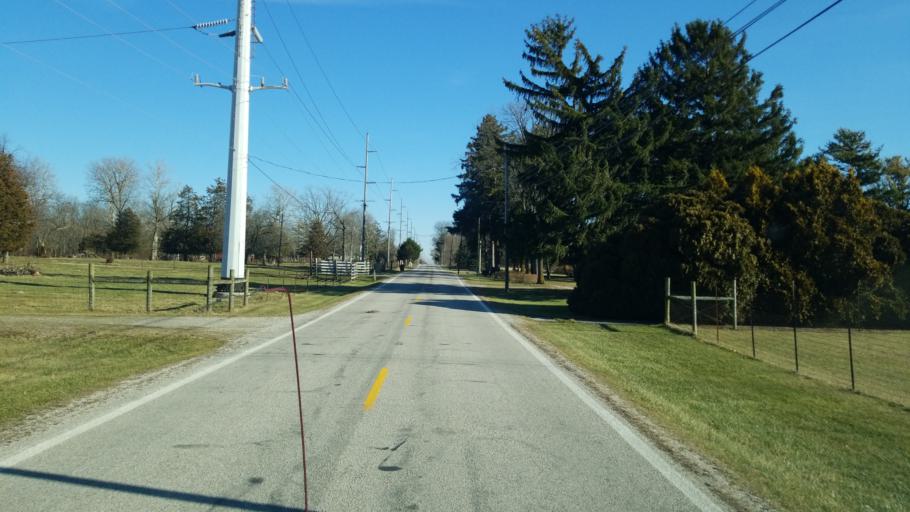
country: US
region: Ohio
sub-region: Wood County
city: Pemberville
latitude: 41.4500
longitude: -83.4444
